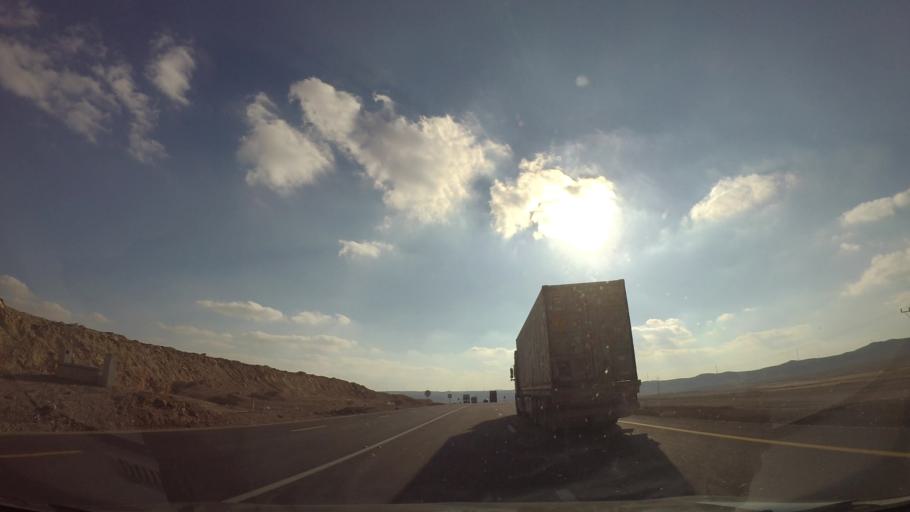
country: JO
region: Karak
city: Karak City
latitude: 31.1271
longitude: 36.0195
